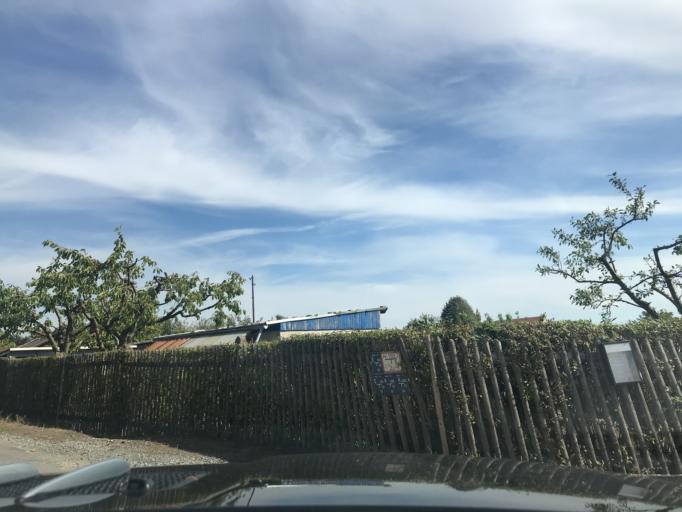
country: DE
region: Thuringia
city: Muehlhausen
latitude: 51.1984
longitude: 10.4526
